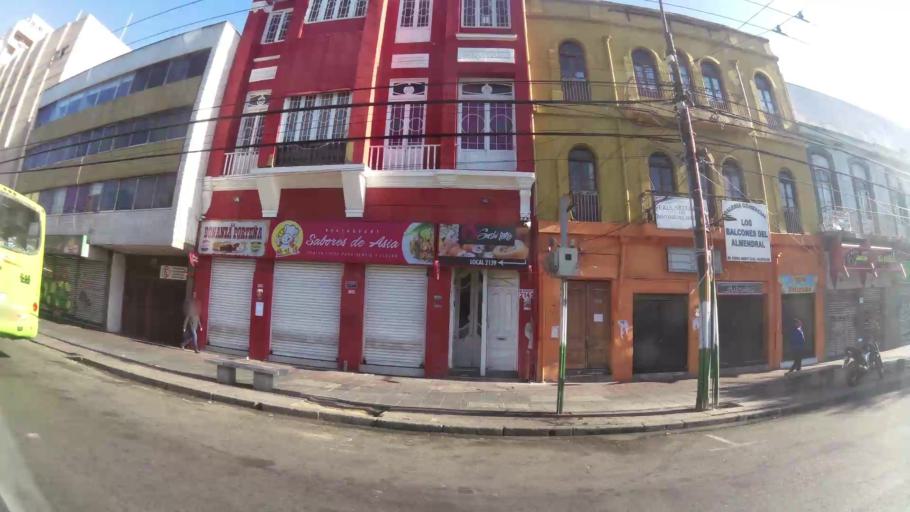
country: CL
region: Valparaiso
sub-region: Provincia de Valparaiso
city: Valparaiso
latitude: -33.0472
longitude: -71.6142
